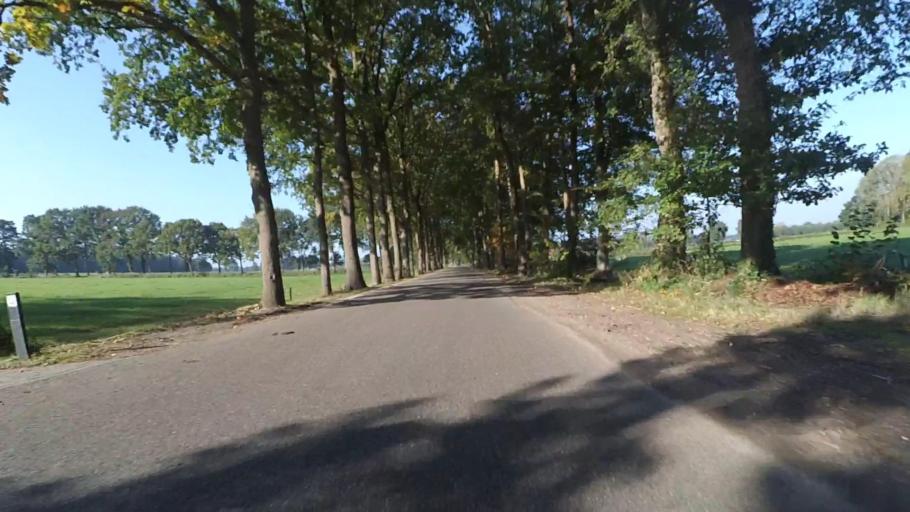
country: NL
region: Gelderland
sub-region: Gemeente Nijkerk
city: Nijkerk
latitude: 52.2167
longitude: 5.5240
